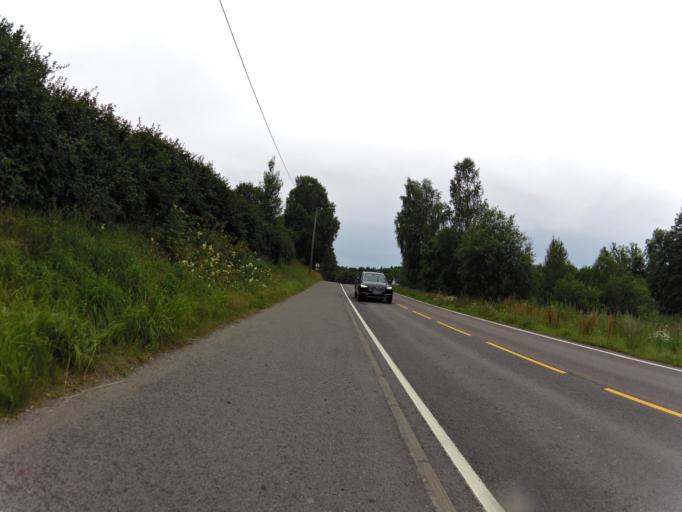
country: NO
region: Ostfold
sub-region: Moss
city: Moss
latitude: 59.4726
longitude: 10.6921
